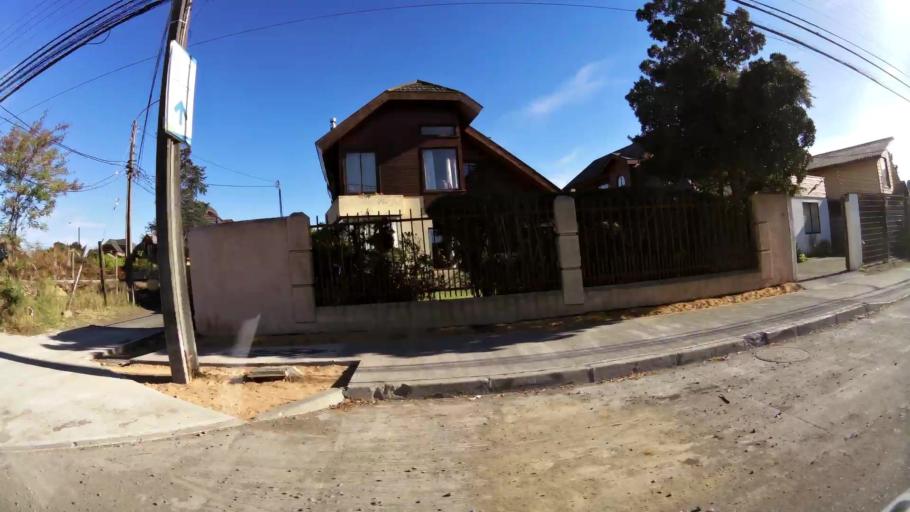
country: CL
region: Biobio
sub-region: Provincia de Concepcion
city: Concepcion
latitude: -36.8320
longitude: -73.1132
